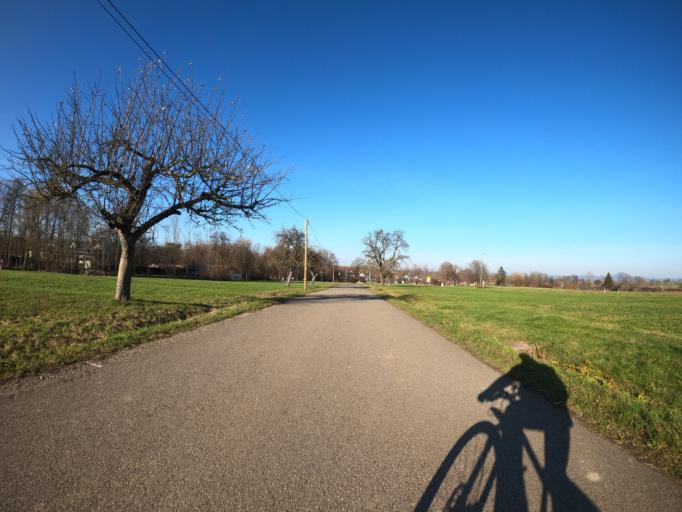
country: DE
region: Baden-Wuerttemberg
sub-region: Regierungsbezirk Stuttgart
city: Heiningen
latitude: 48.6556
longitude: 9.6561
